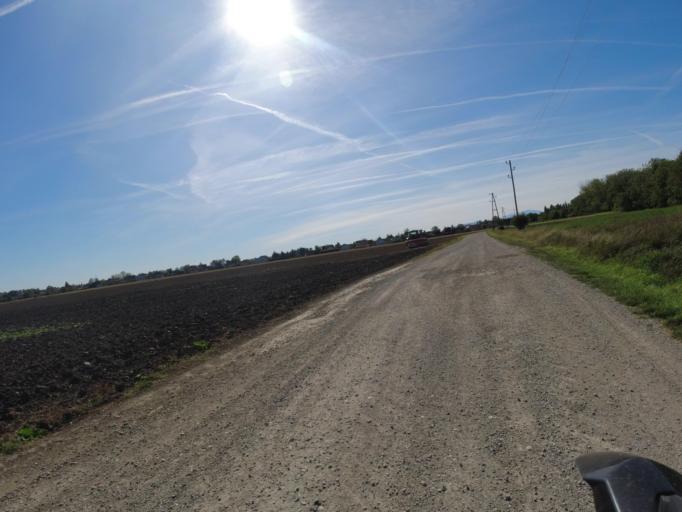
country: AT
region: Lower Austria
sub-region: Politischer Bezirk Modling
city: Guntramsdorf
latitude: 48.0237
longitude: 16.3227
